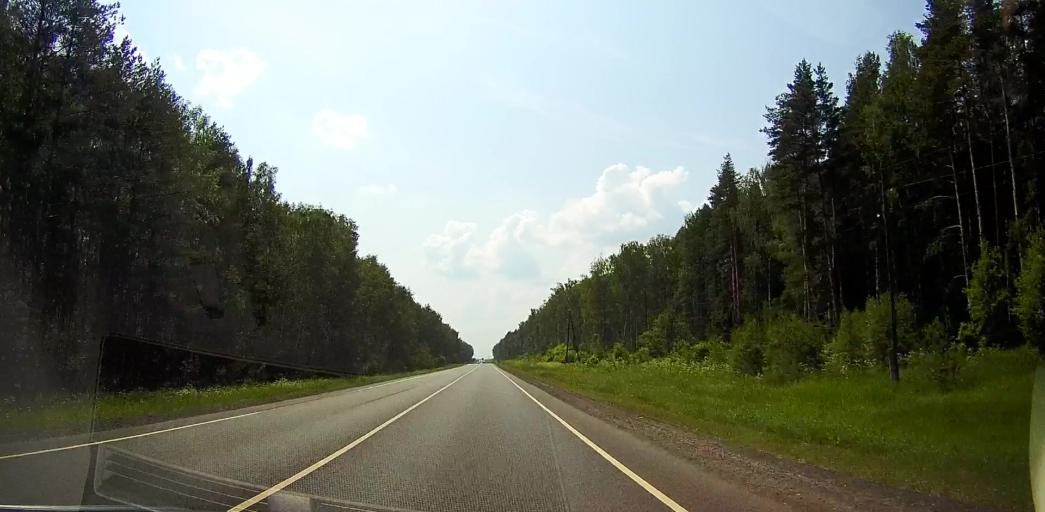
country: RU
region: Moskovskaya
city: Meshcherino
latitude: 55.1664
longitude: 38.3222
